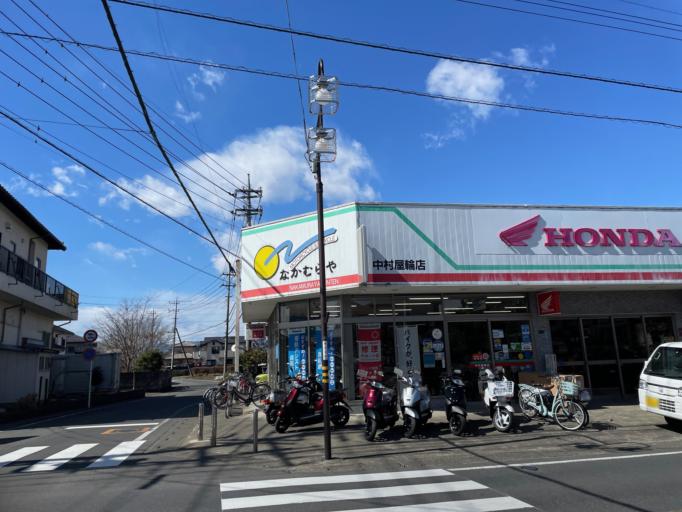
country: JP
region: Saitama
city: Sakado
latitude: 35.9752
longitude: 139.4172
